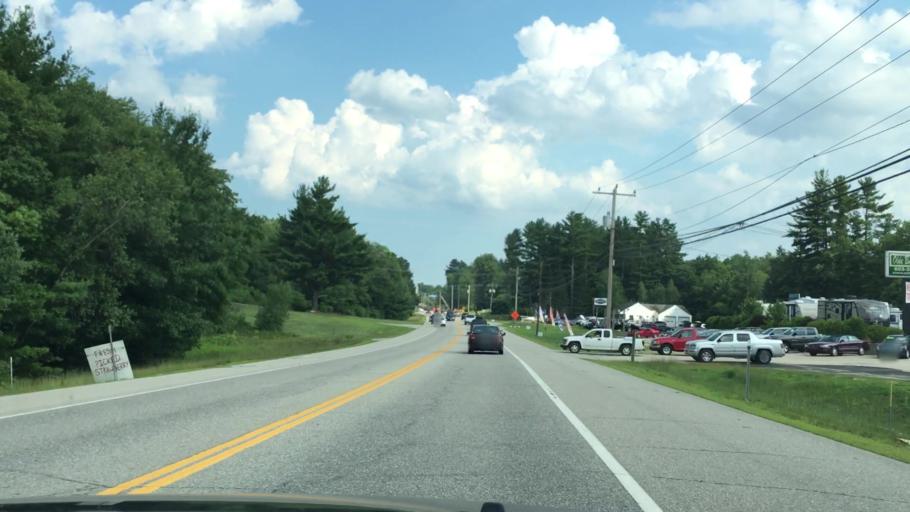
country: US
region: New Hampshire
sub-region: Strafford County
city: Rochester
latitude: 43.3412
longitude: -71.0183
